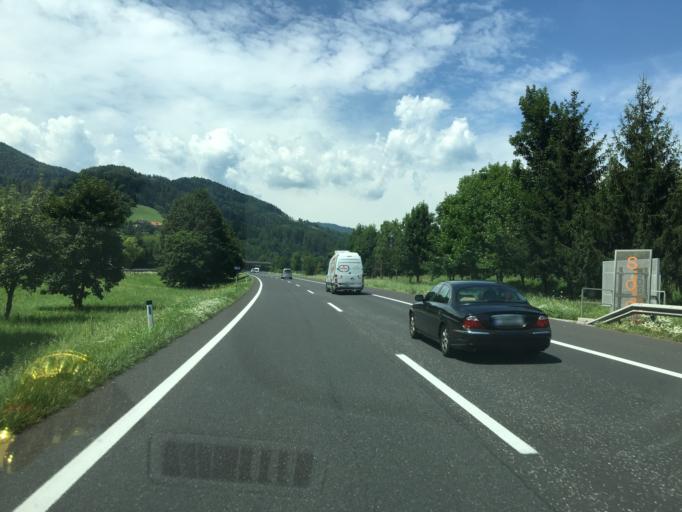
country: AT
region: Styria
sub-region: Politischer Bezirk Graz-Umgebung
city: Deutschfeistritz
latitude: 47.2051
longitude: 15.3192
